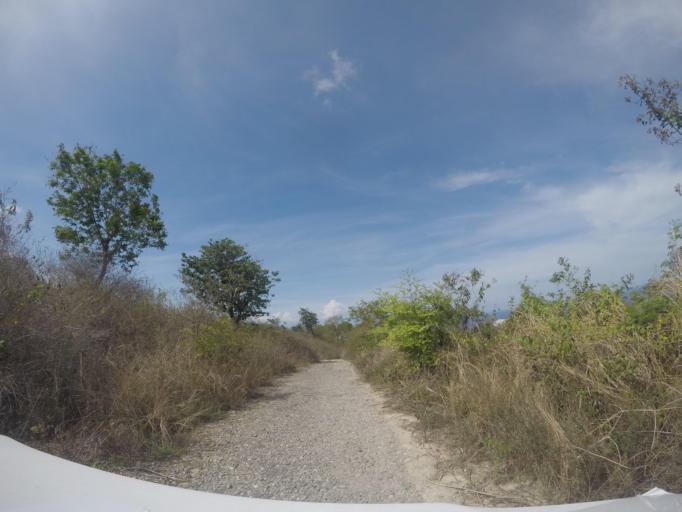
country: TL
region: Baucau
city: Baucau
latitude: -8.4674
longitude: 126.4705
